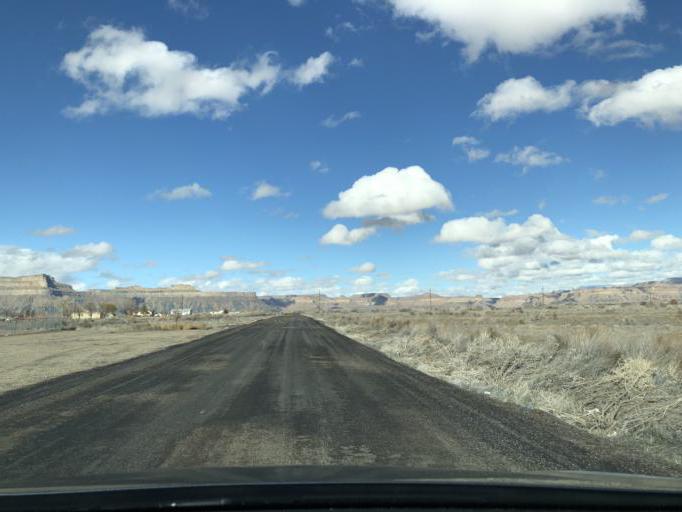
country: US
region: Utah
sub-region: Carbon County
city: East Carbon City
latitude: 38.9972
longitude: -110.1699
